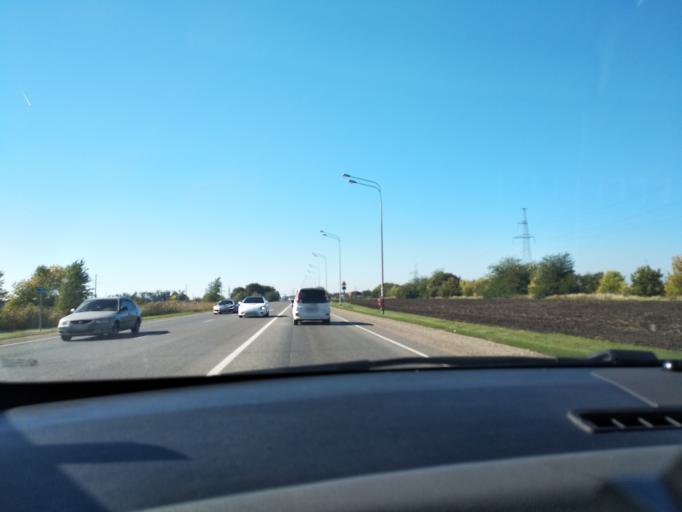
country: RU
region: Krasnodarskiy
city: Agronom
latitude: 45.1708
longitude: 39.0949
